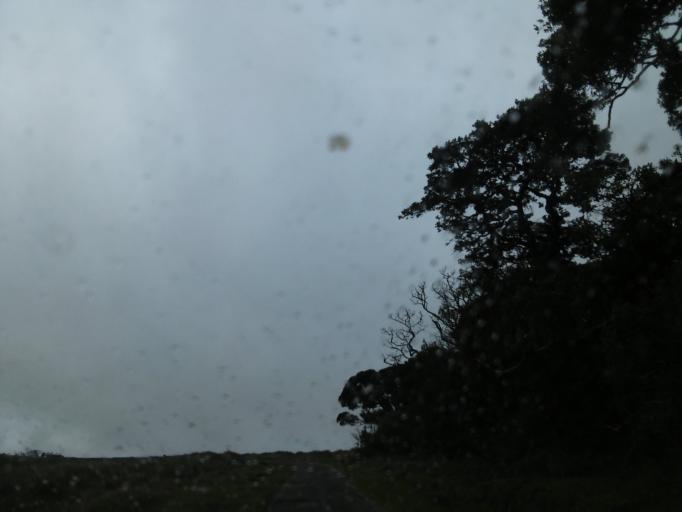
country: LK
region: Uva
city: Haputale
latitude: 6.7939
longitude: 80.8242
